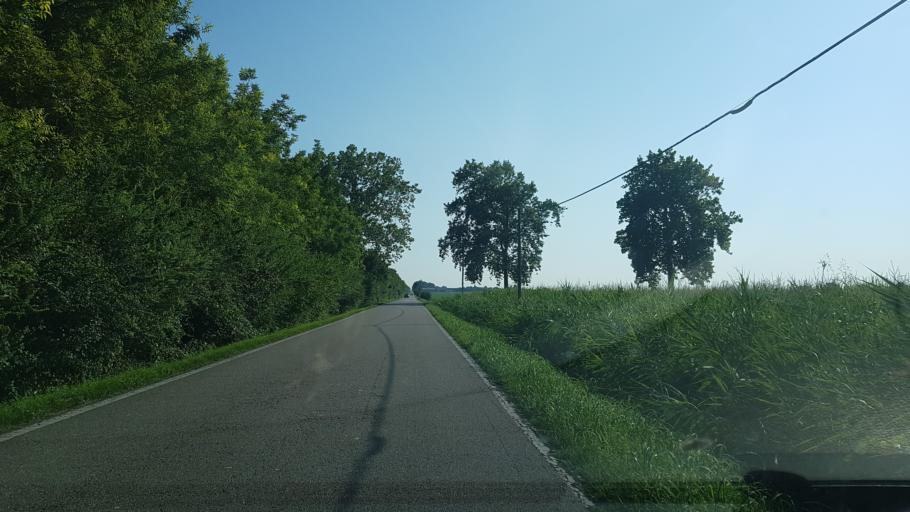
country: IT
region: Veneto
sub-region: Provincia di Venezia
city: San Giorgio di Livenza
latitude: 45.6399
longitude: 12.7900
